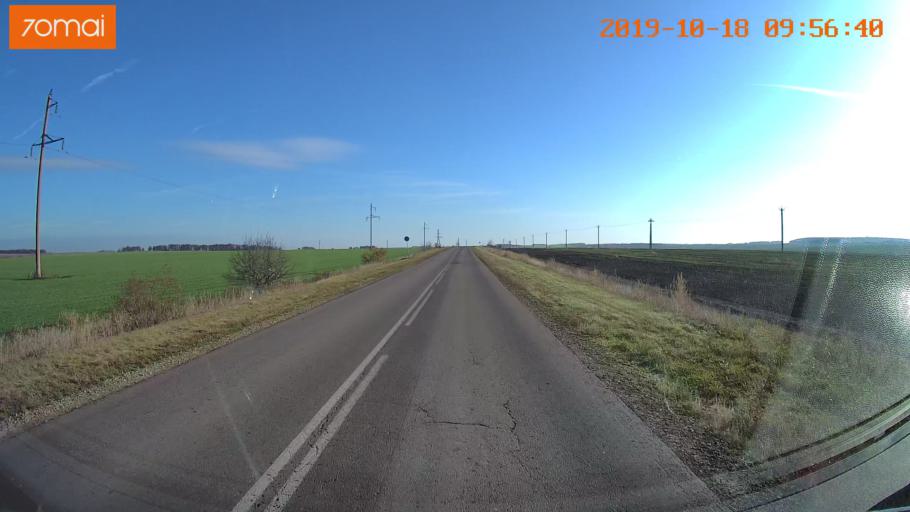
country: RU
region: Tula
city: Kurkino
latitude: 53.3750
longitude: 38.3961
